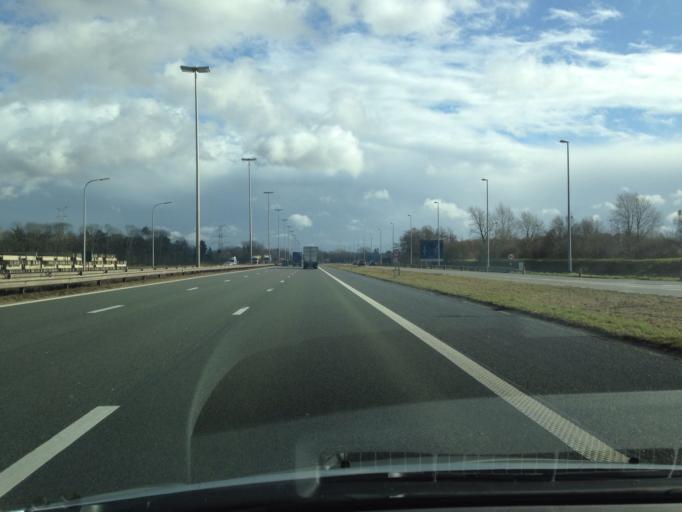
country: BE
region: Flanders
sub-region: Provincie West-Vlaanderen
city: Jabbeke
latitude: 51.1852
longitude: 3.1101
